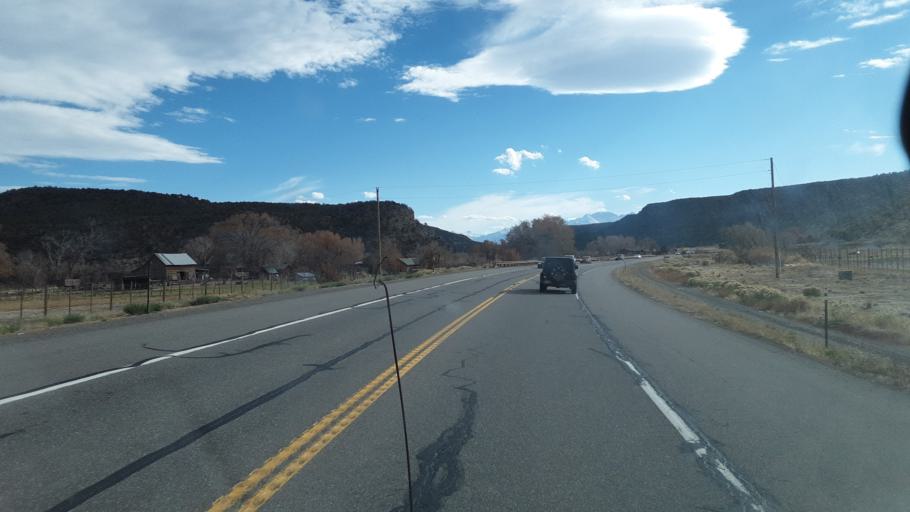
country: US
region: Colorado
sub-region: Montrose County
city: Montrose
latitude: 38.3077
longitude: -107.7733
